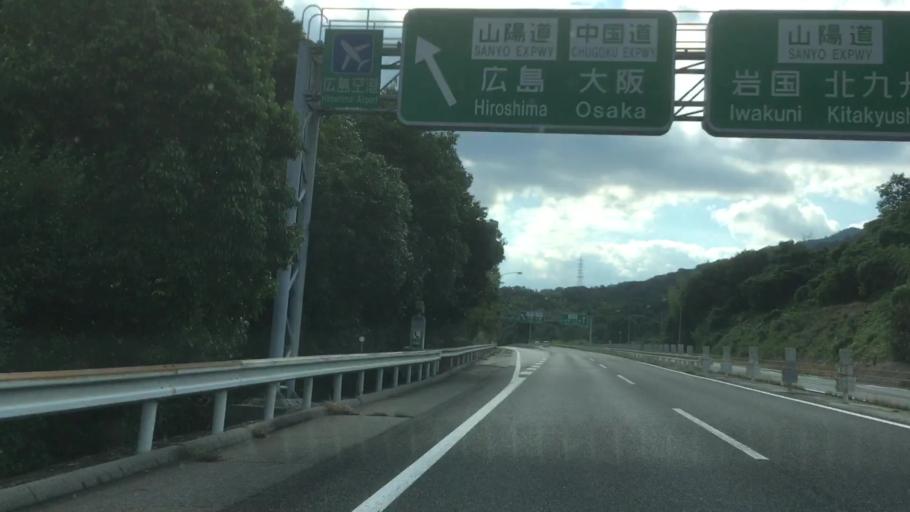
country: JP
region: Hiroshima
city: Hatsukaichi
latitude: 34.3391
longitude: 132.2988
